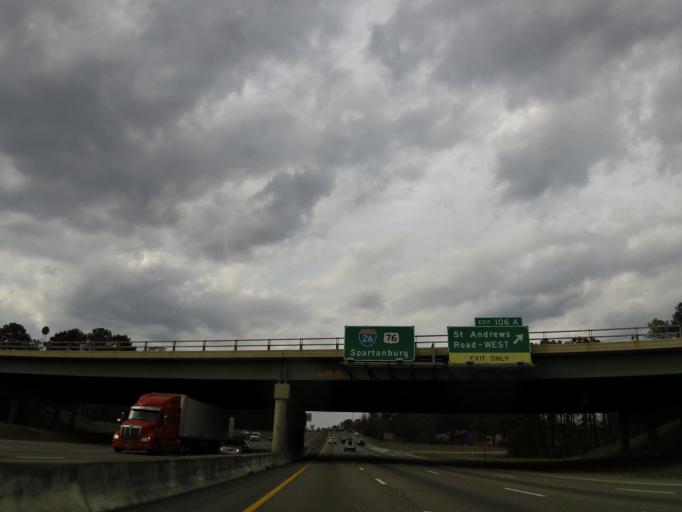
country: US
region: South Carolina
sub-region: Lexington County
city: Saint Andrews
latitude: 34.0442
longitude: -81.1176
